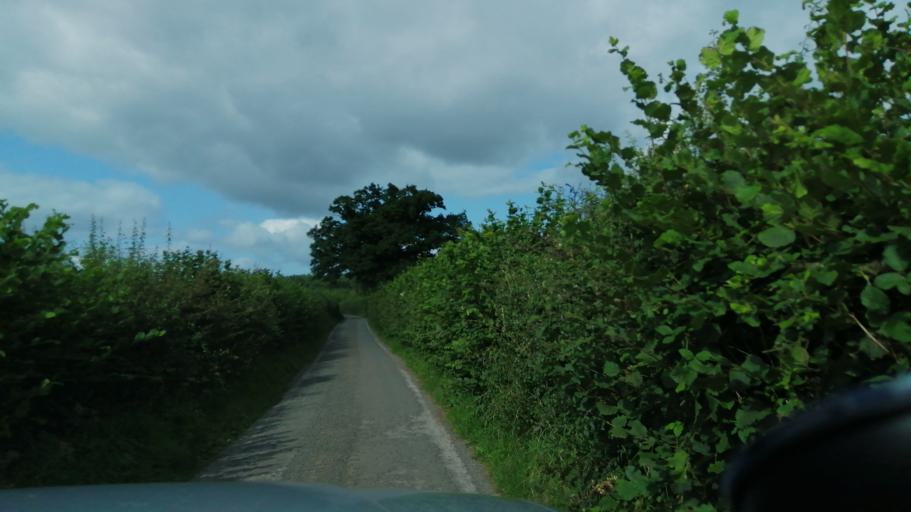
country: GB
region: England
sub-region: Herefordshire
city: Kinnersley
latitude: 52.1333
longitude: -2.9443
